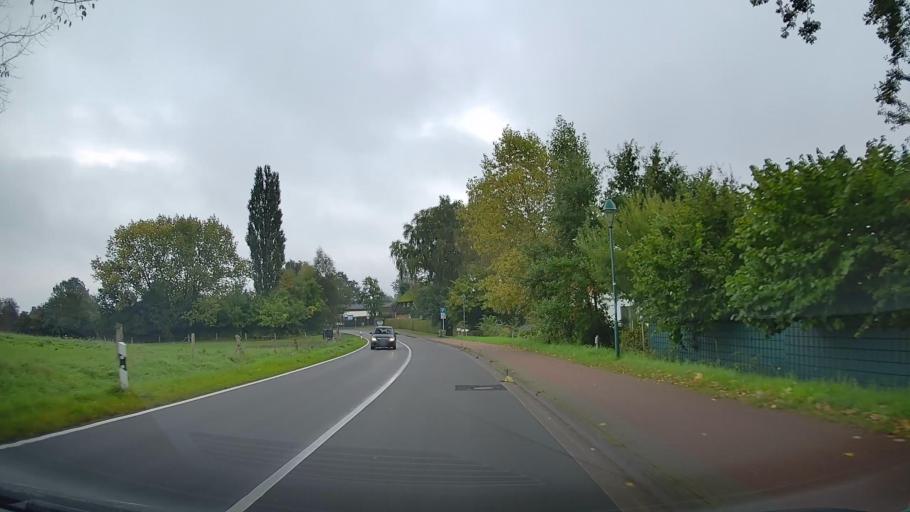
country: DE
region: Mecklenburg-Vorpommern
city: Ostseebad Boltenhagen
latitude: 53.9413
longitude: 11.2398
